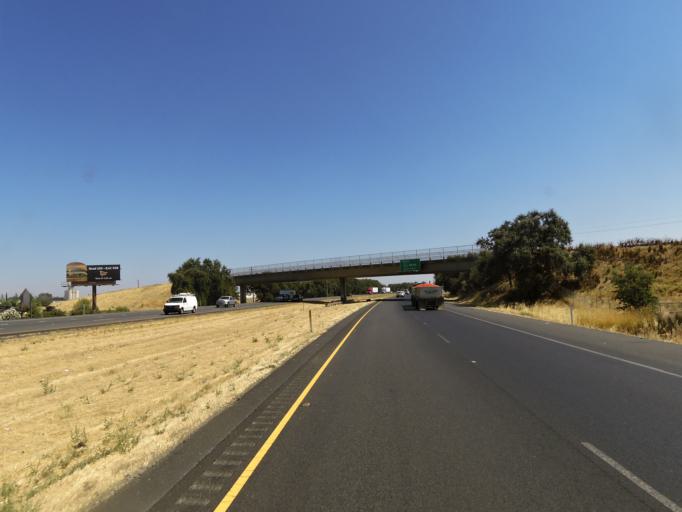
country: US
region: California
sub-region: Yolo County
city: Woodland
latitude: 38.6927
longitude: -121.7576
